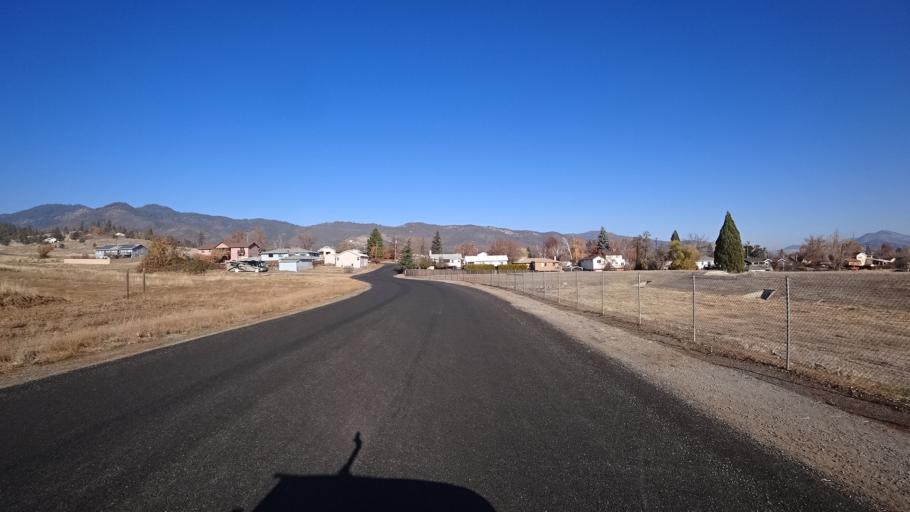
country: US
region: California
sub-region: Siskiyou County
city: Yreka
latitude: 41.7264
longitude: -122.6463
